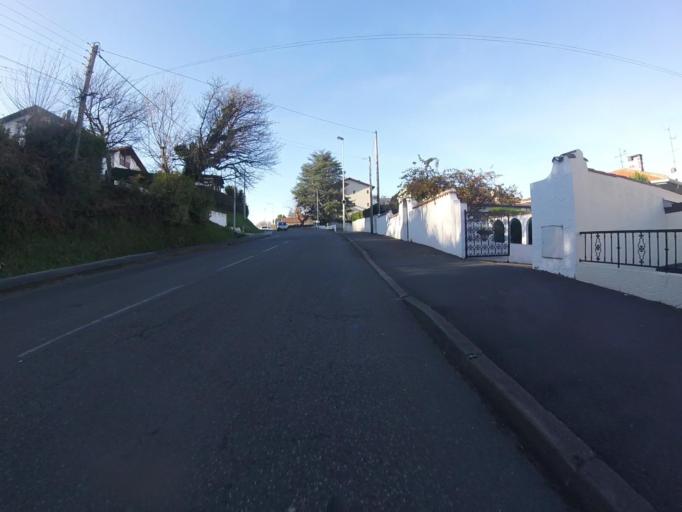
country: FR
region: Aquitaine
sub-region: Departement des Pyrenees-Atlantiques
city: Hendaye
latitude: 43.3558
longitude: -1.7671
